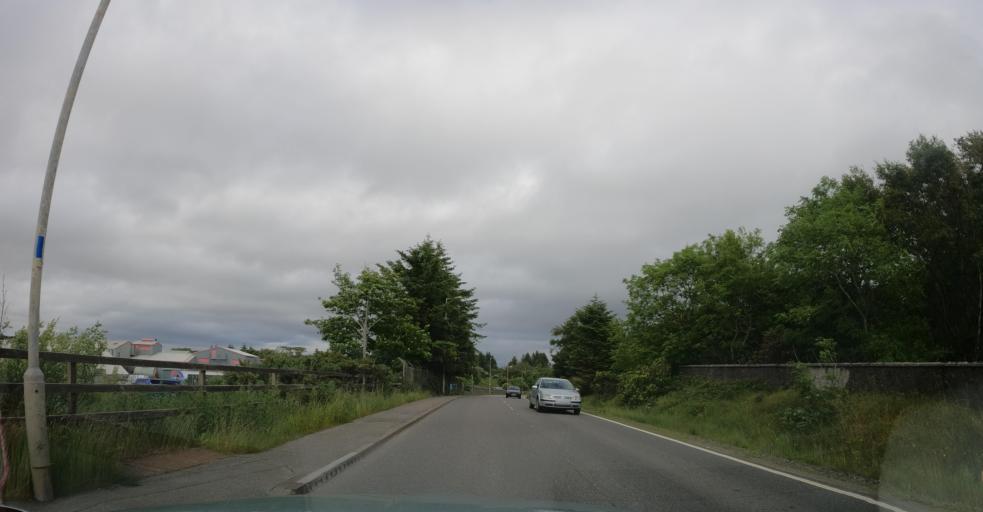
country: GB
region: Scotland
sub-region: Eilean Siar
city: Isle of Lewis
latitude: 58.2179
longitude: -6.4068
